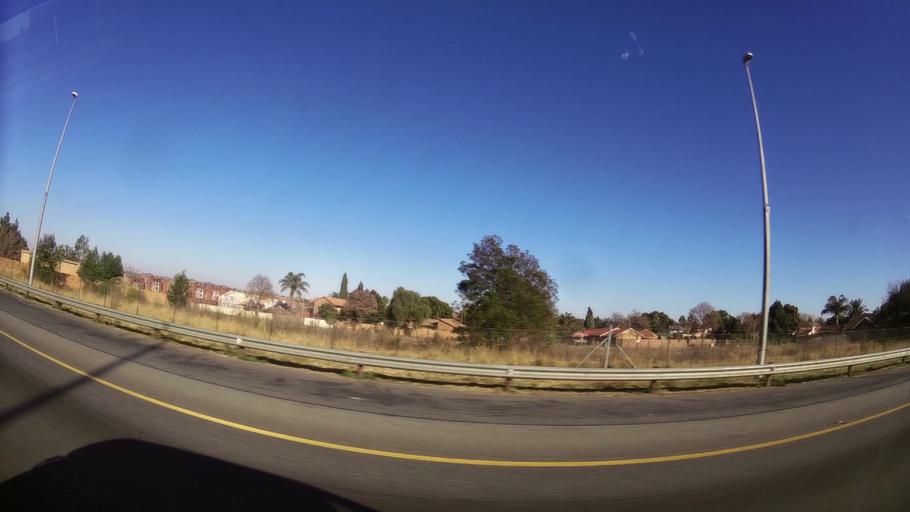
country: ZA
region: Gauteng
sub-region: City of Tshwane Metropolitan Municipality
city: Centurion
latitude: -25.8495
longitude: 28.2510
